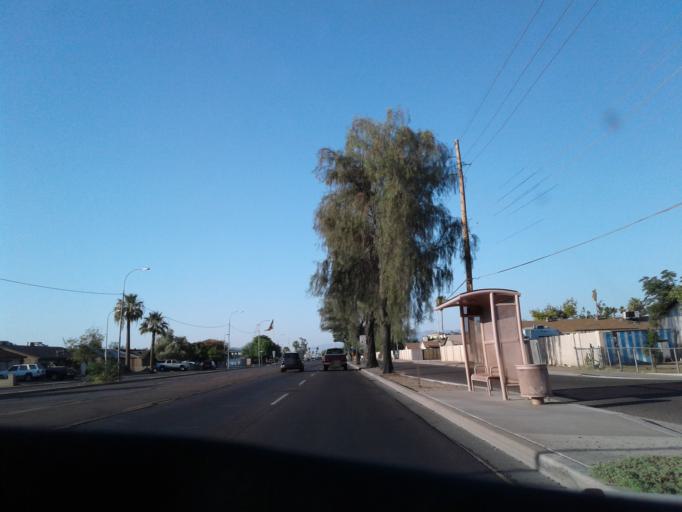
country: US
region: Arizona
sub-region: Maricopa County
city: Glendale
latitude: 33.4690
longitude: -112.1865
